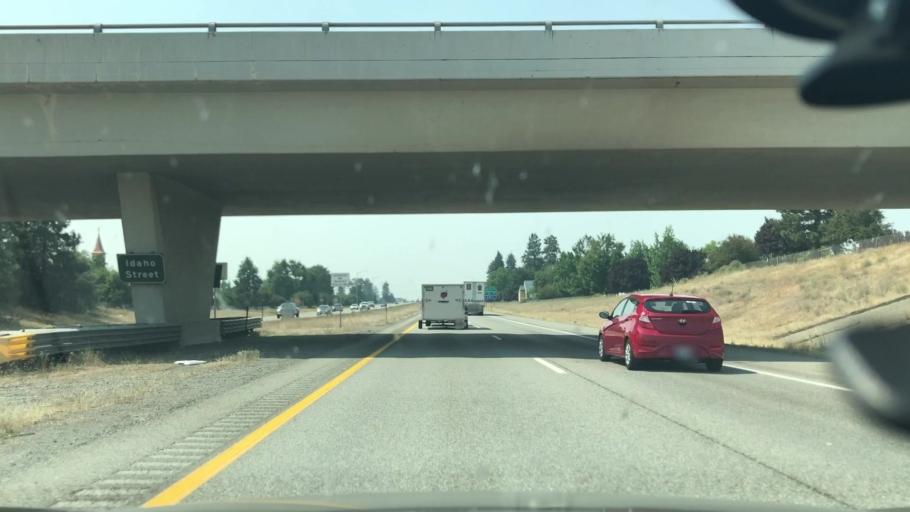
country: US
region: Idaho
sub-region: Kootenai County
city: Post Falls
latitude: 47.7127
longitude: -116.9370
